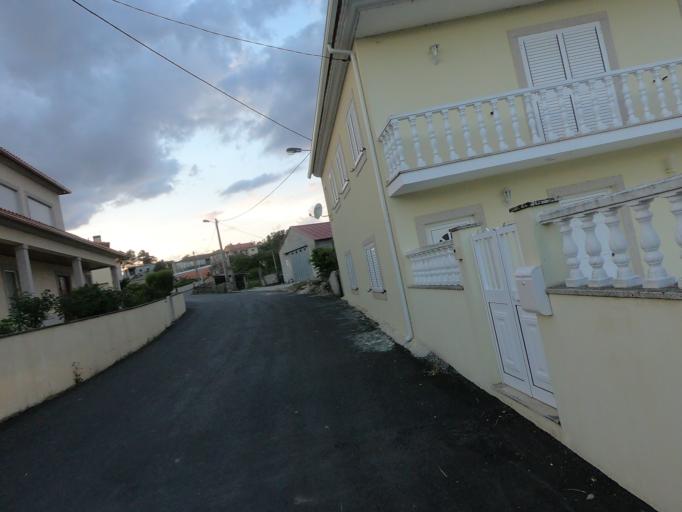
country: PT
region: Vila Real
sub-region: Vila Real
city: Vila Real
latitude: 41.2669
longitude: -7.7139
